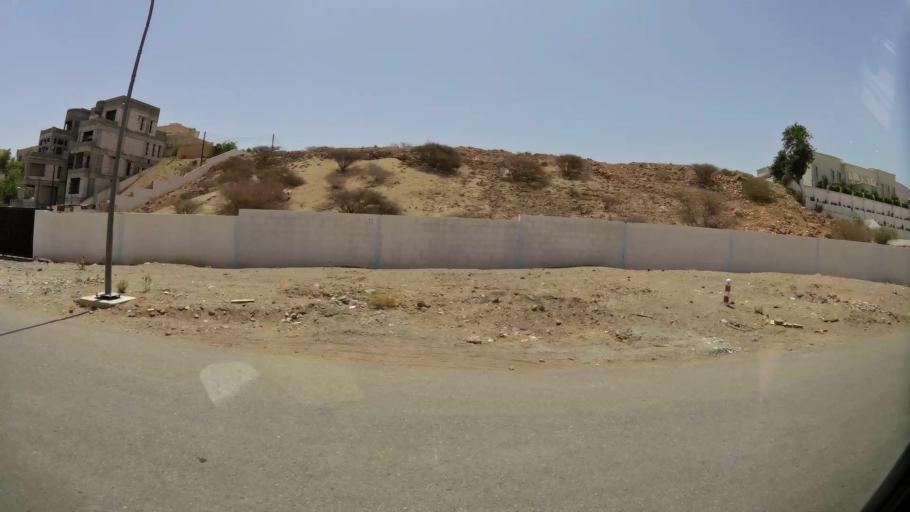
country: OM
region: Muhafazat Masqat
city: Bawshar
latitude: 23.5882
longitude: 58.4500
